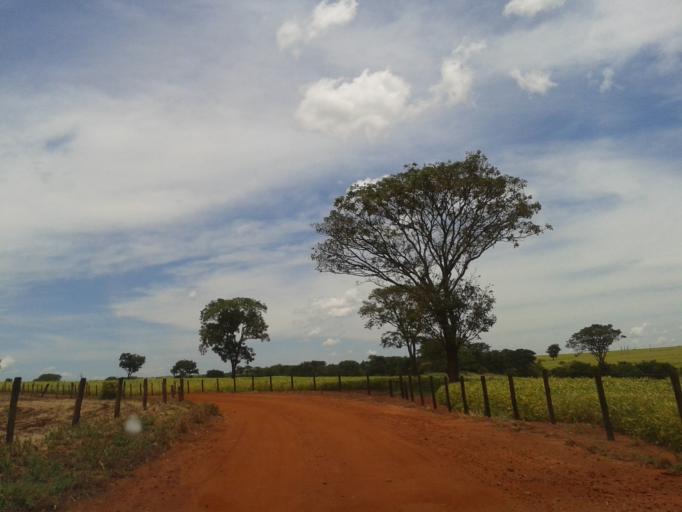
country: BR
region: Minas Gerais
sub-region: Capinopolis
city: Capinopolis
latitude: -18.6998
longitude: -49.7120
